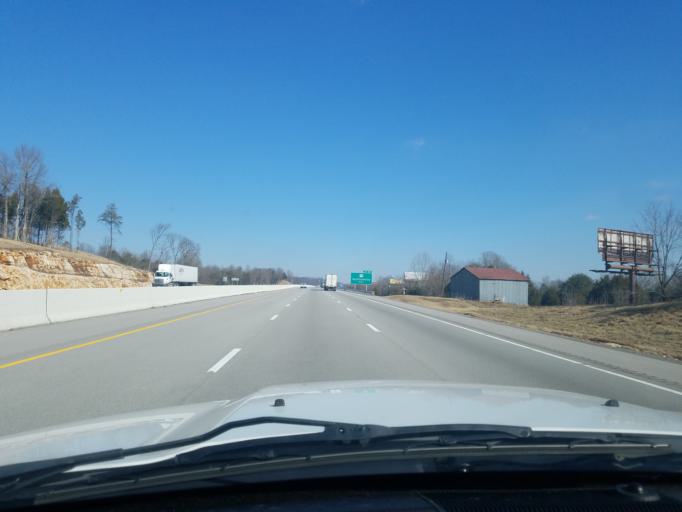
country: US
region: Kentucky
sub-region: Hart County
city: Munfordville
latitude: 37.2834
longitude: -85.9082
